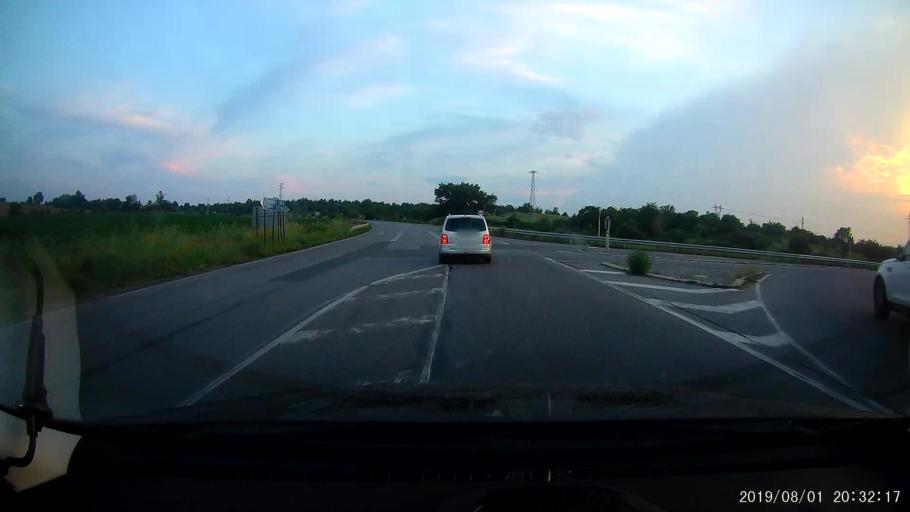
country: BG
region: Yambol
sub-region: Obshtina Elkhovo
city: Elkhovo
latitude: 42.1239
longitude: 26.5315
